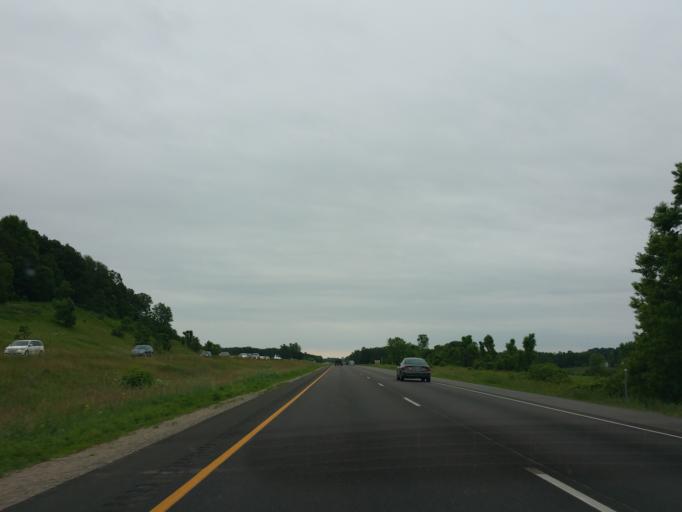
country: US
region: Wisconsin
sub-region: Eau Claire County
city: Fall Creek
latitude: 44.6904
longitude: -91.3356
